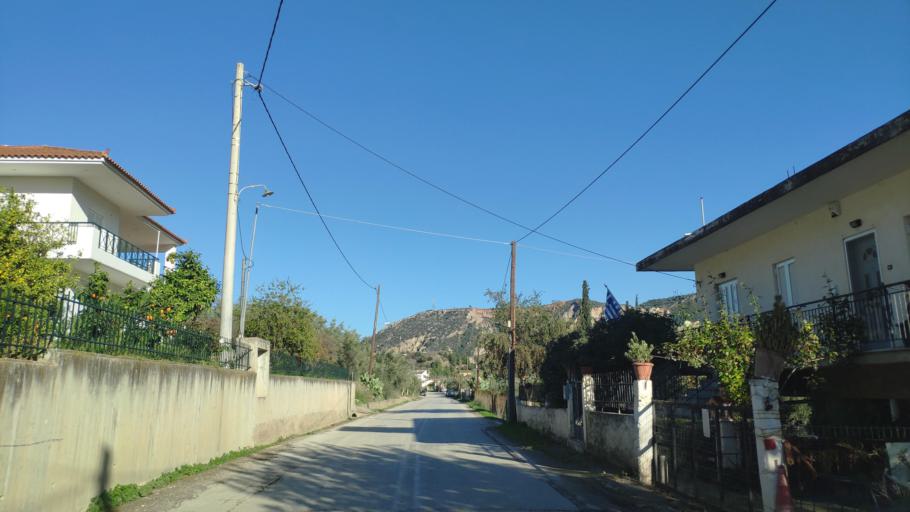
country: GR
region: Peloponnese
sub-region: Nomos Korinthias
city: Xylokastro
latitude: 38.0556
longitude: 22.6058
